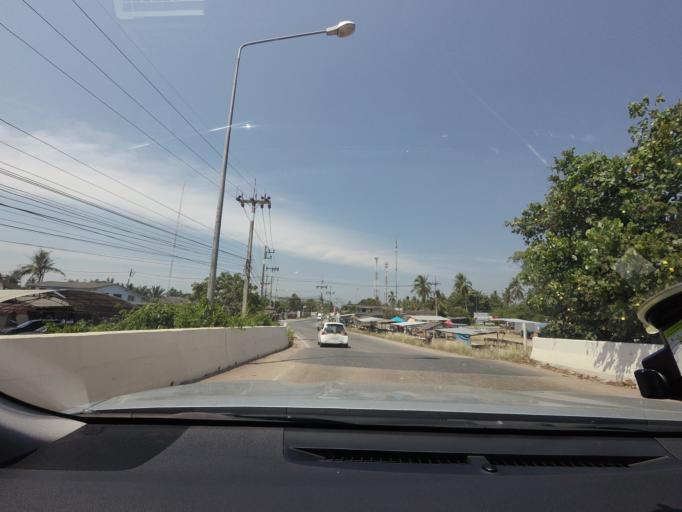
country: TH
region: Surat Thani
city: Phunphin
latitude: 9.1917
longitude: 99.2537
